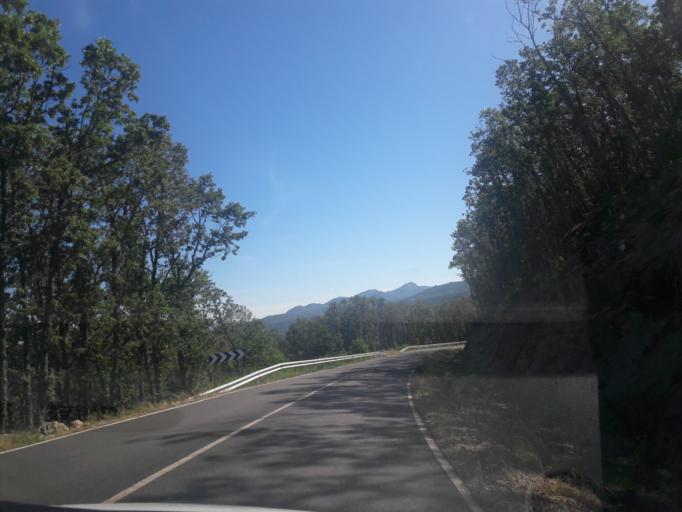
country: ES
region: Castille and Leon
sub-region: Provincia de Salamanca
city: Montemayor del Rio
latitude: 40.3420
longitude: -5.8790
